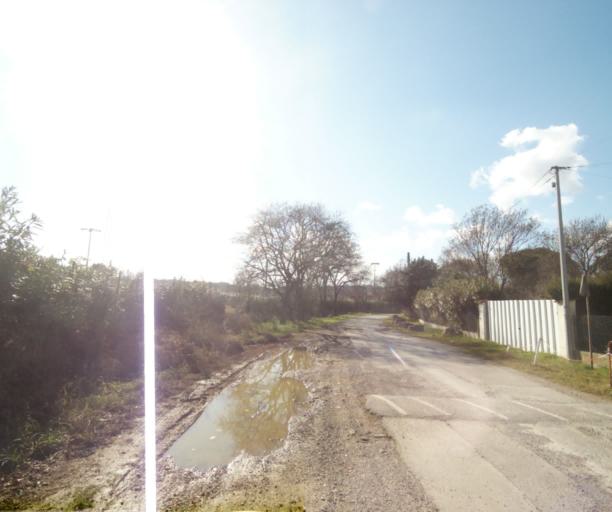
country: FR
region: Provence-Alpes-Cote d'Azur
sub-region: Departement des Alpes-Maritimes
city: Biot
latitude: 43.6156
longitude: 7.1222
